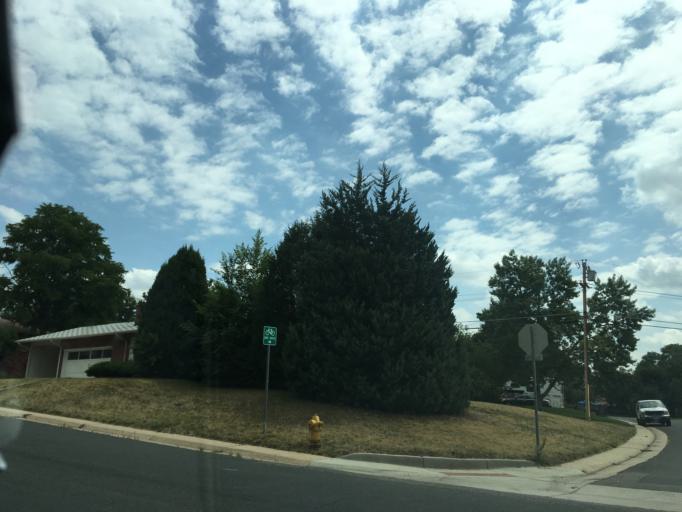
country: US
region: Colorado
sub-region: Arapahoe County
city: Sheridan
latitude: 39.6638
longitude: -105.0403
